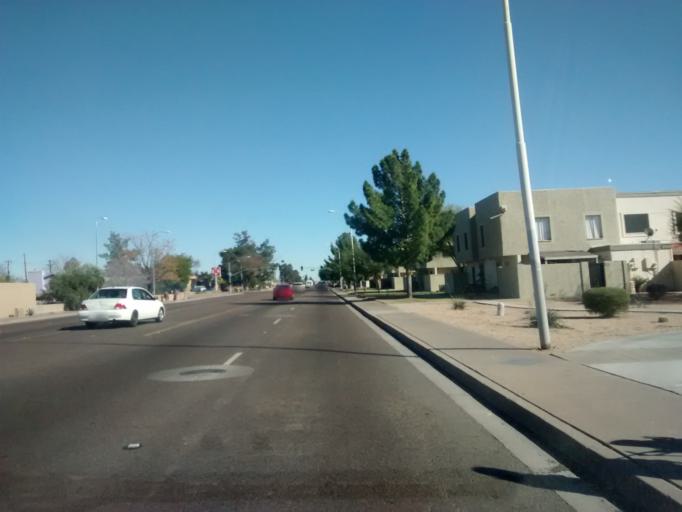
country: US
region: Arizona
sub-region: Maricopa County
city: Glendale
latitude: 33.5239
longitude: -112.1620
